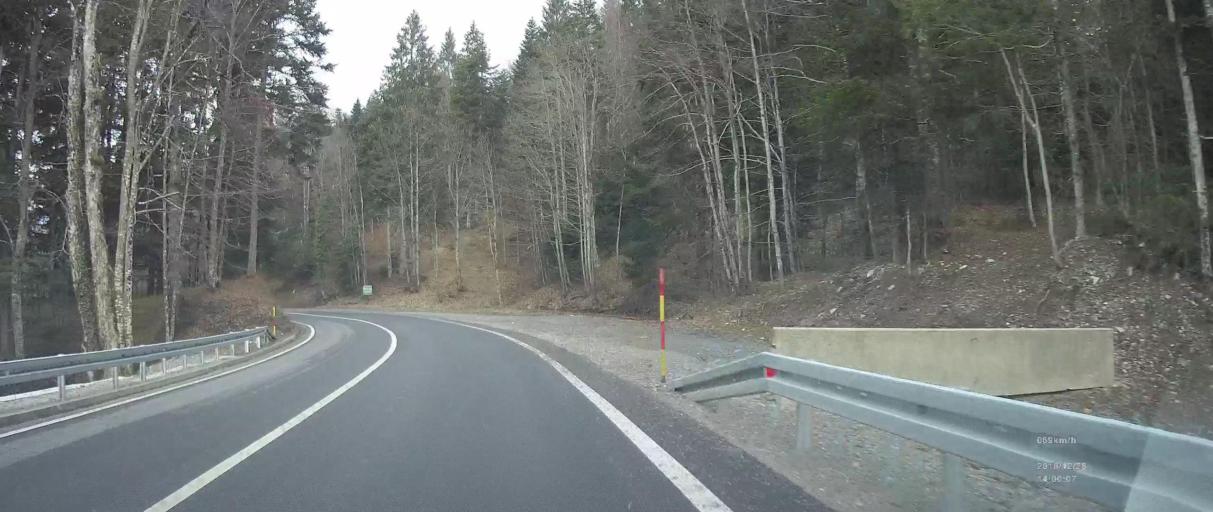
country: SI
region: Kostel
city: Kostel
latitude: 45.4086
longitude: 14.9141
